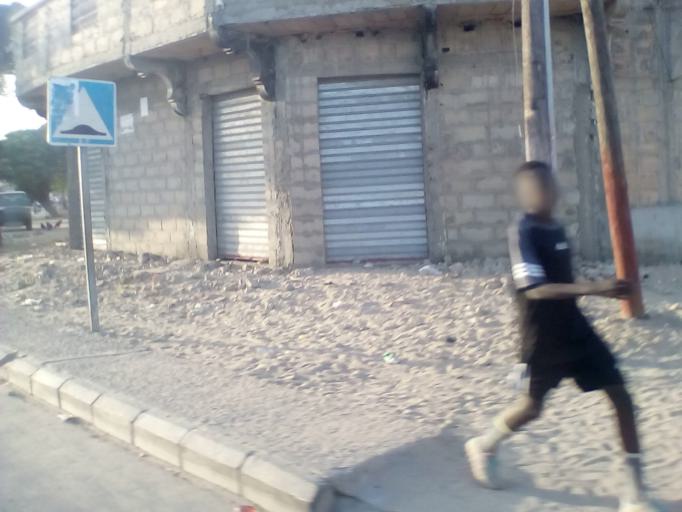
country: SN
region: Saint-Louis
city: Saint-Louis
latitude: 16.0185
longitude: -16.4926
